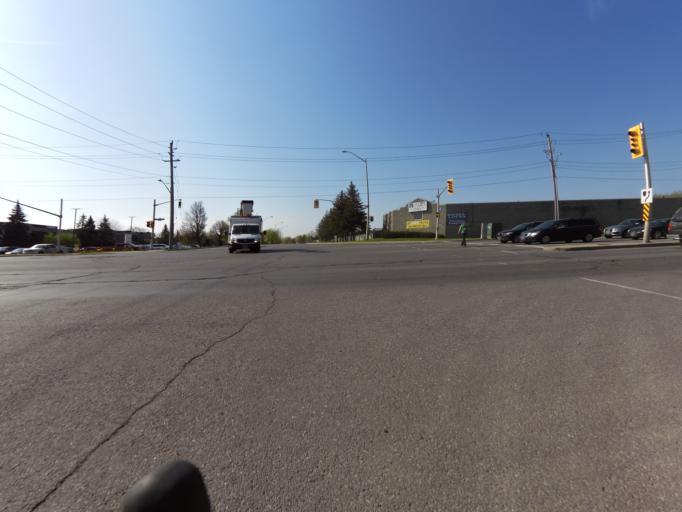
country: CA
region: Ontario
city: Ottawa
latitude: 45.3330
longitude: -75.7291
